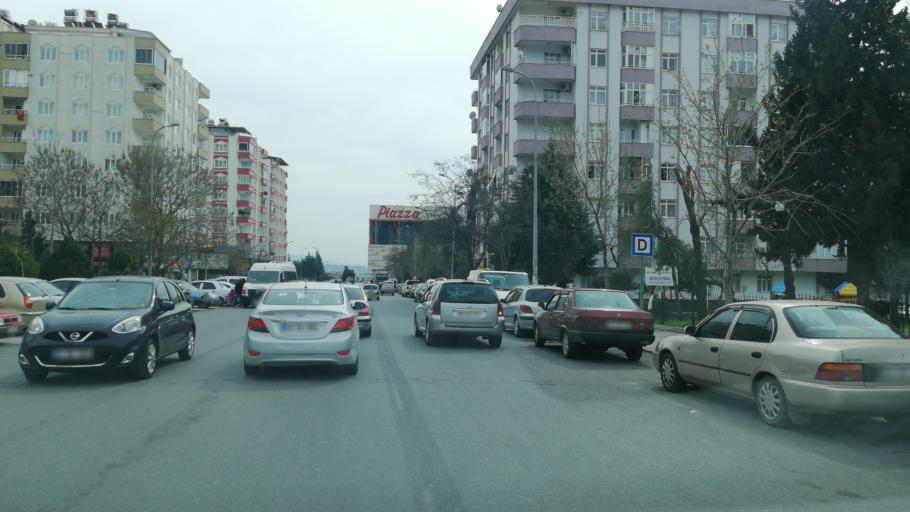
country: TR
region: Kahramanmaras
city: Kahramanmaras
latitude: 37.5728
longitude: 36.9242
